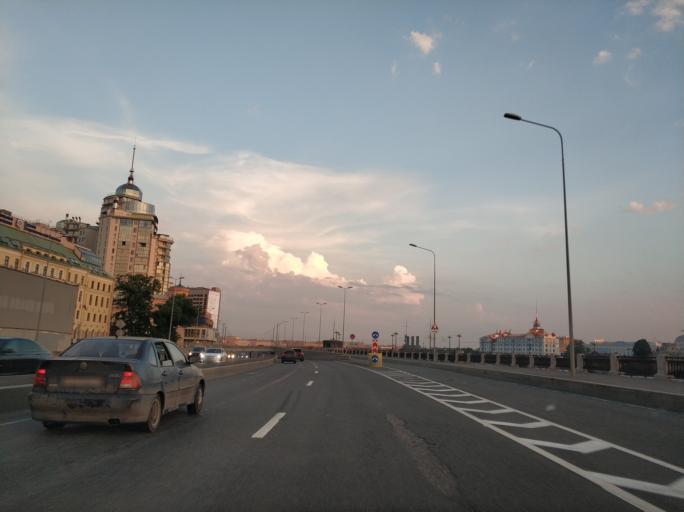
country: RU
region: Leningrad
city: Sampsonievskiy
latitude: 59.9605
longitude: 30.3382
